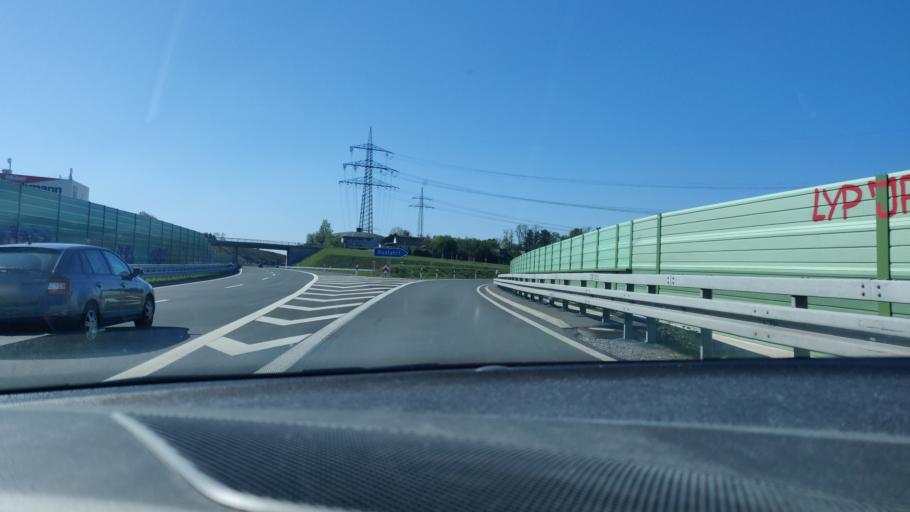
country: DE
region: North Rhine-Westphalia
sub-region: Regierungsbezirk Dusseldorf
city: Velbert
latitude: 51.3314
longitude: 7.0133
